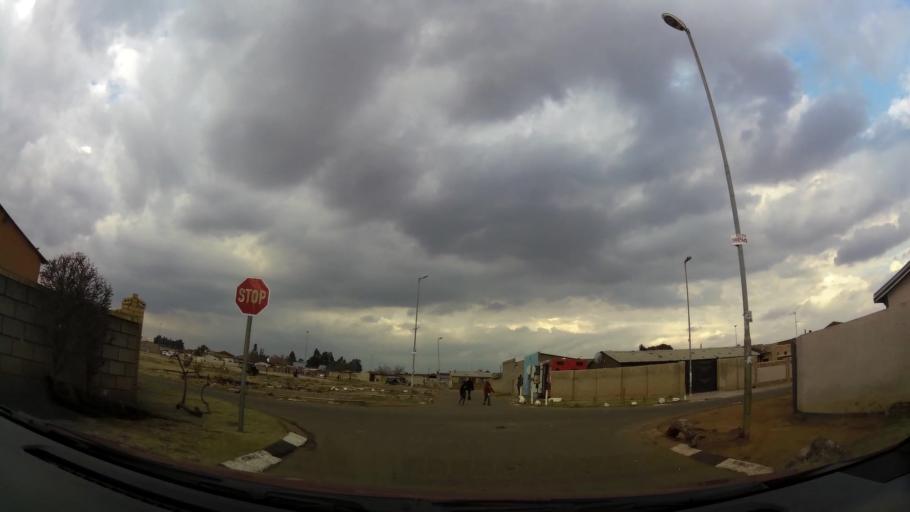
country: ZA
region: Gauteng
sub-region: City of Johannesburg Metropolitan Municipality
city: Soweto
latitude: -26.2441
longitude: 27.8180
